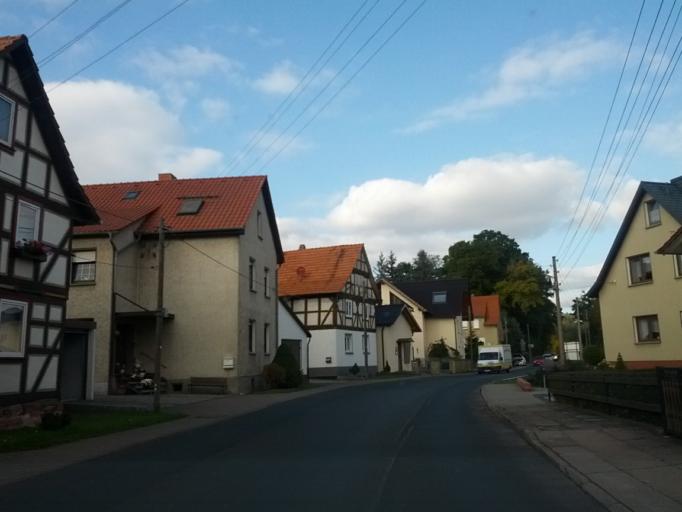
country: DE
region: Thuringia
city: Marksuhl
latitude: 50.9312
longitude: 10.1539
